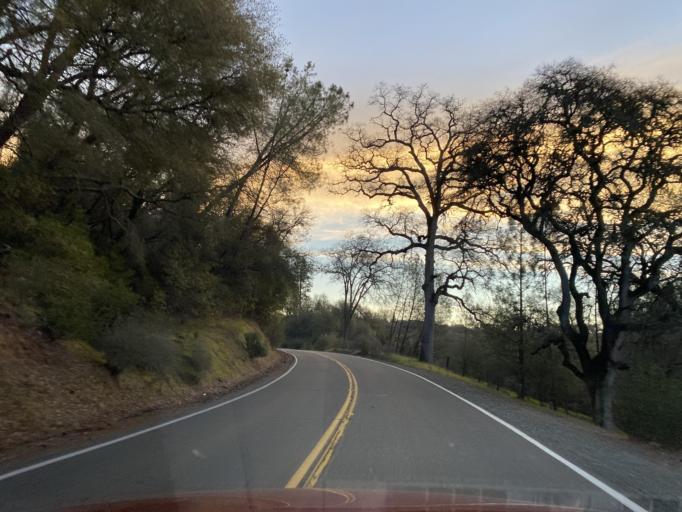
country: US
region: California
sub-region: Amador County
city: Plymouth
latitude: 38.4903
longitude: -120.7961
